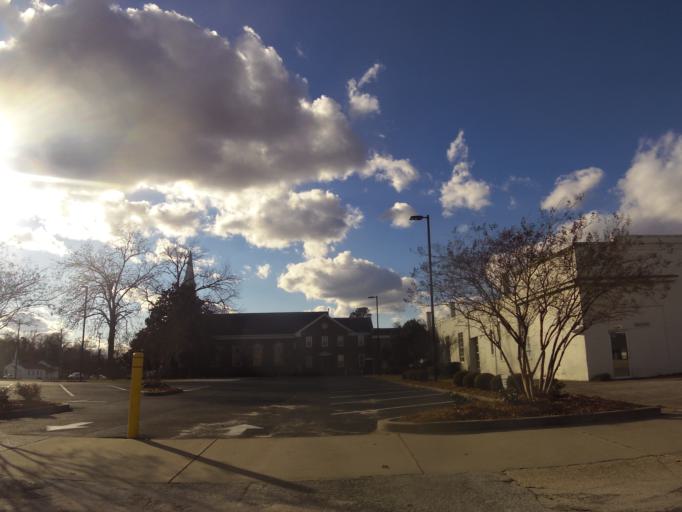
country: US
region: South Carolina
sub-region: Clarendon County
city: Manning
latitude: 33.6959
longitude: -80.2120
